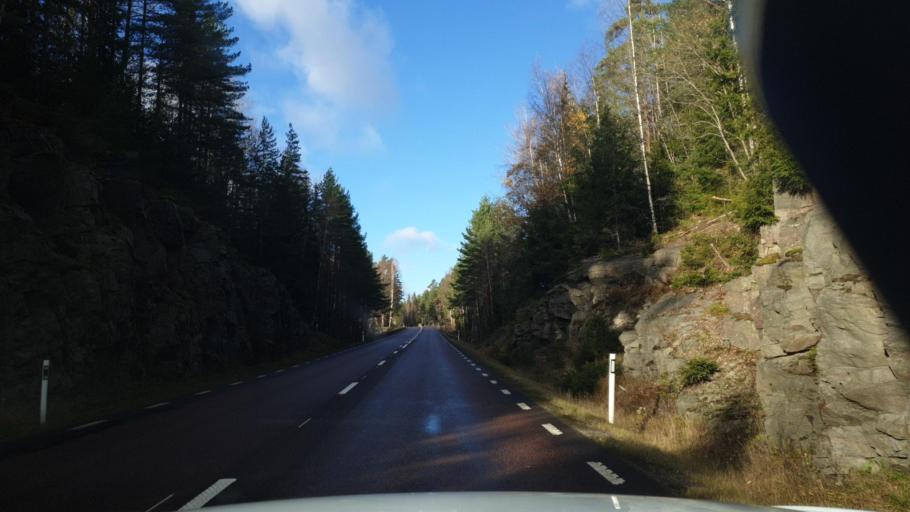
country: SE
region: Vaermland
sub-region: Arvika Kommun
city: Arvika
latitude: 59.5917
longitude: 12.6461
